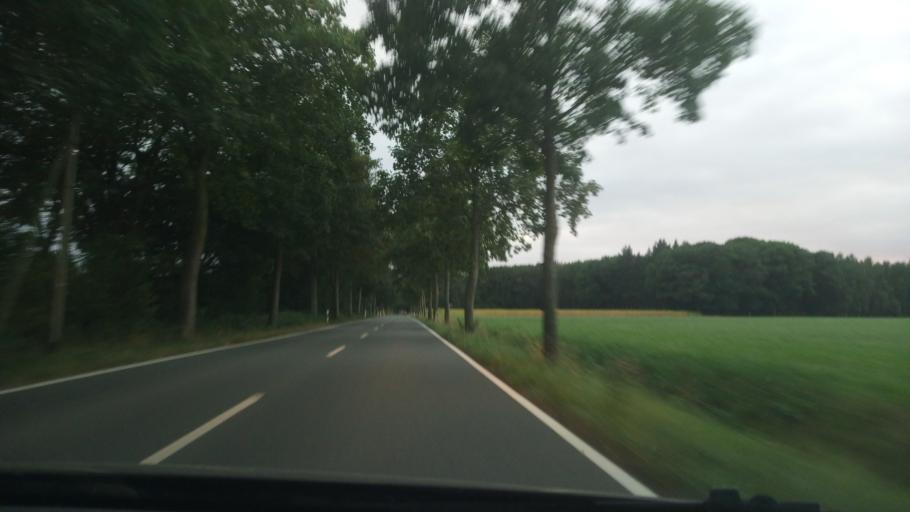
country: DE
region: North Rhine-Westphalia
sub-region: Regierungsbezirk Munster
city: Legden
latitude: 51.9760
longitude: 7.1123
